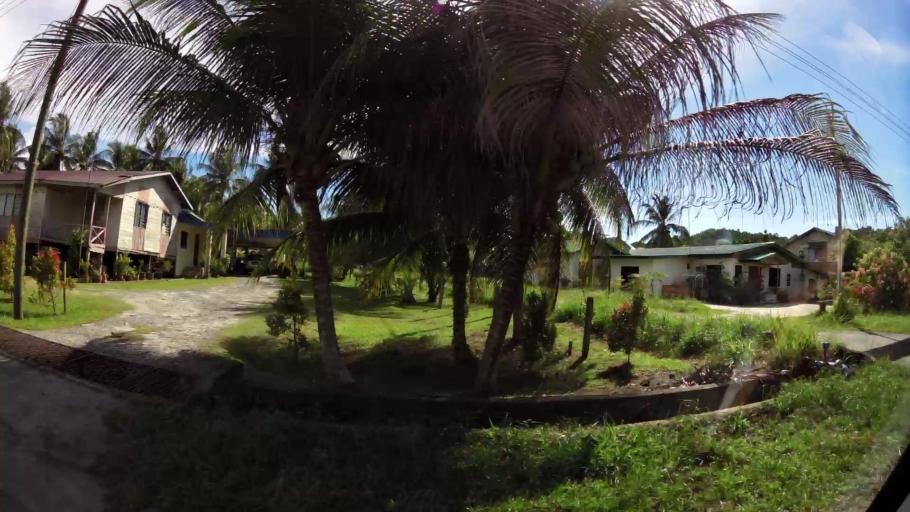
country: BN
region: Brunei and Muara
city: Bandar Seri Begawan
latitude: 5.0233
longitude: 115.0456
